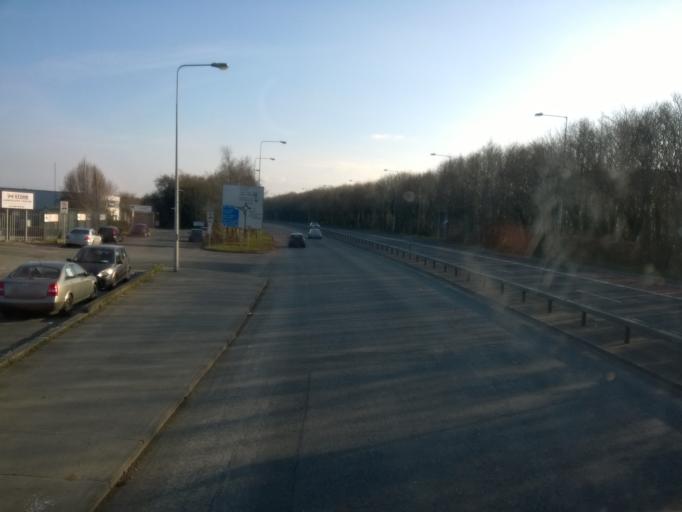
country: IE
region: Leinster
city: Kinsealy-Drinan
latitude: 53.4322
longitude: -6.2298
